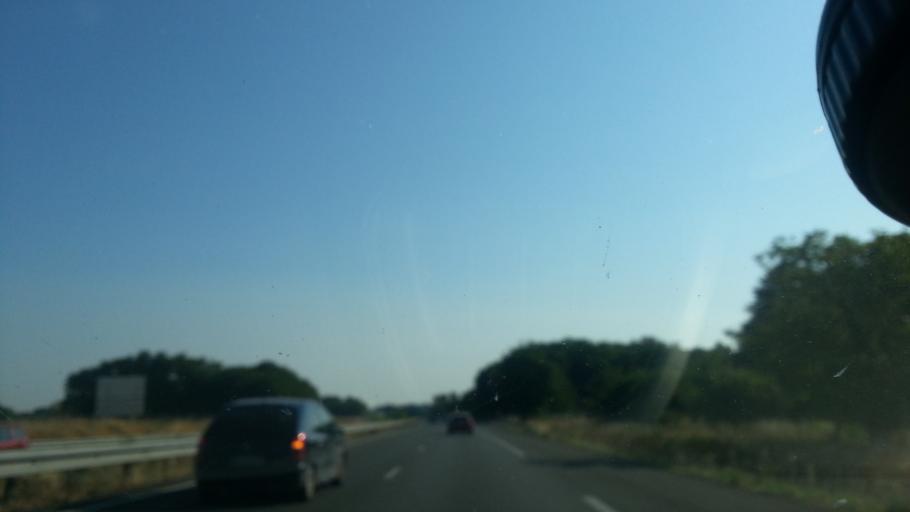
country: FR
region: Poitou-Charentes
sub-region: Departement de la Vienne
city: Naintre
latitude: 46.7756
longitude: 0.4926
